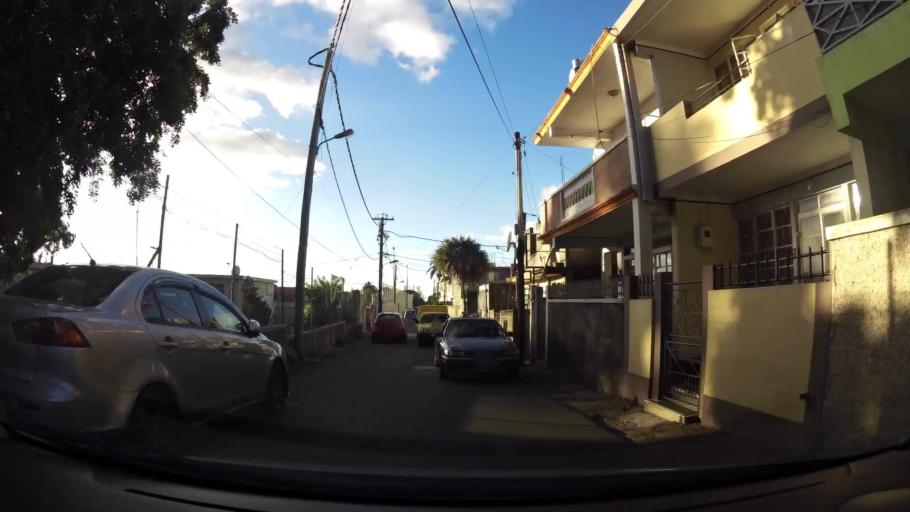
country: MU
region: Plaines Wilhems
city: Quatre Bornes
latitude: -20.2507
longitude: 57.4617
